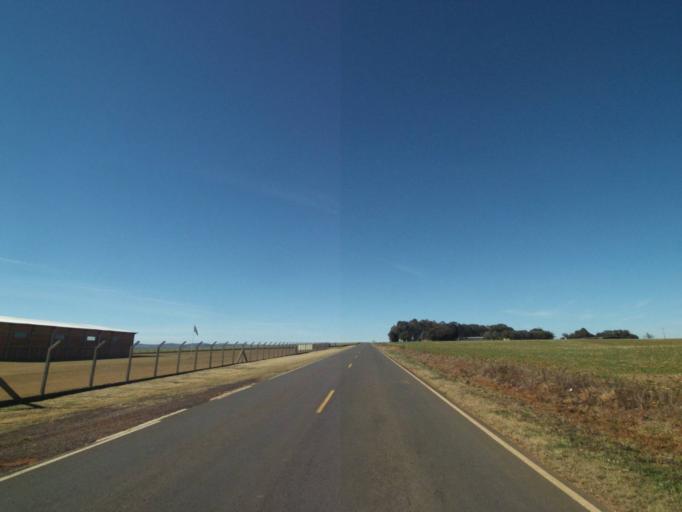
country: BR
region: Parana
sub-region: Tibagi
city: Tibagi
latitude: -24.5495
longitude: -50.2946
